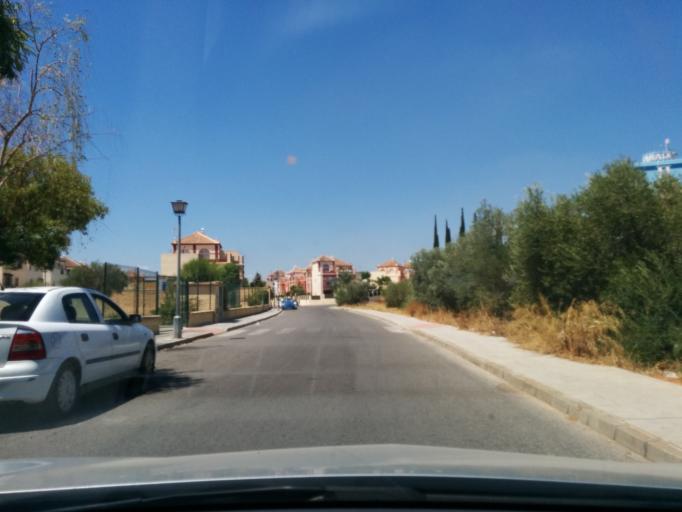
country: ES
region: Andalusia
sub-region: Provincia de Sevilla
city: Benacazon
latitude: 37.3590
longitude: -6.1971
